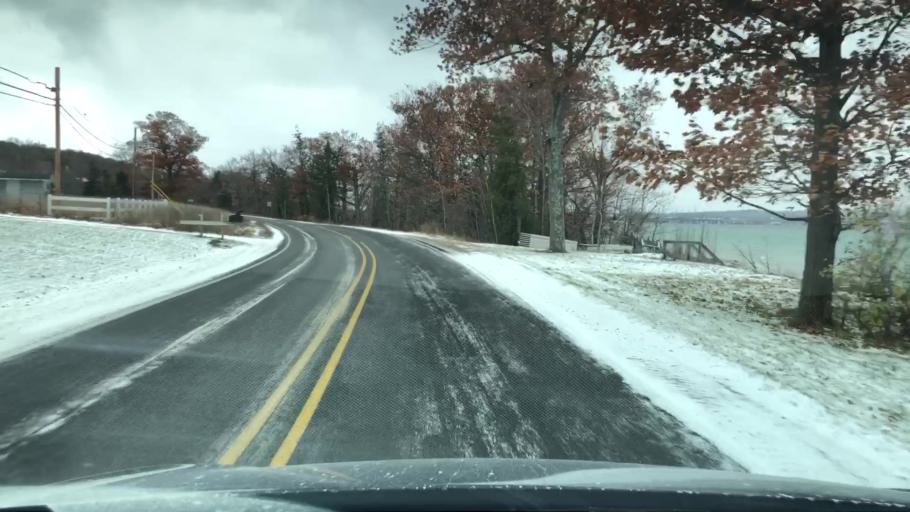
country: US
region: Michigan
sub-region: Grand Traverse County
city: Traverse City
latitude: 44.8093
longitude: -85.5808
